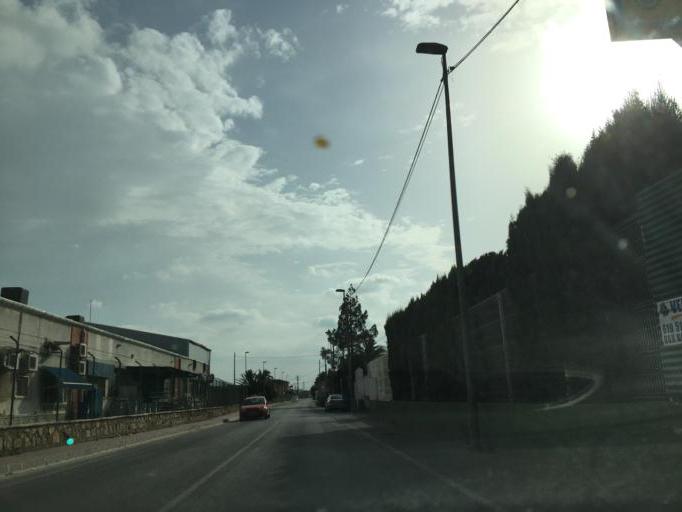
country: ES
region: Murcia
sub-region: Murcia
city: Murcia
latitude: 38.0133
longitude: -1.1040
